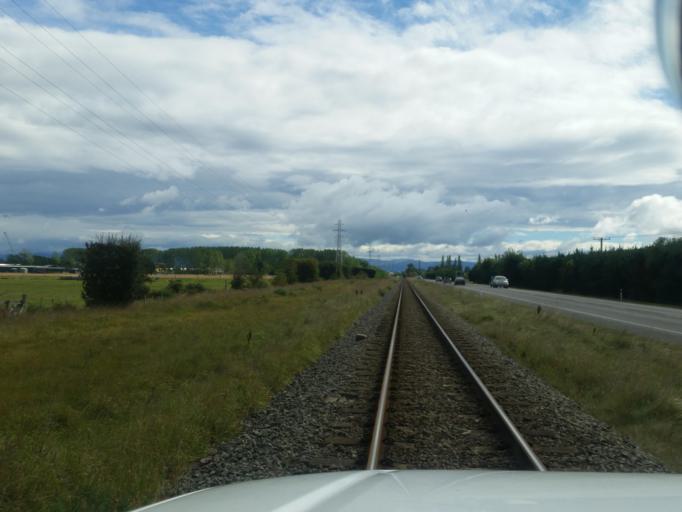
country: NZ
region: Canterbury
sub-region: Waimakariri District
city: Kaiapoi
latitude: -43.3387
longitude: 172.6111
